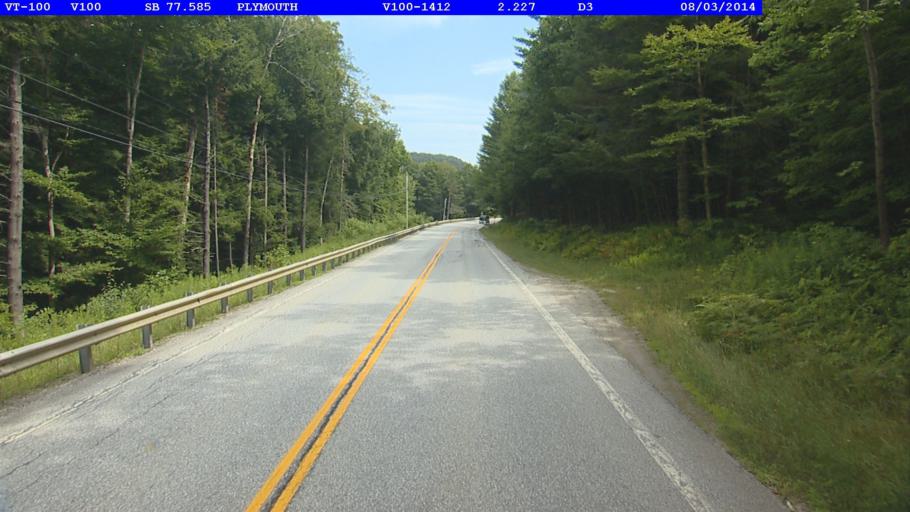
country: US
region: Vermont
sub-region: Windsor County
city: Woodstock
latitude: 43.4935
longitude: -72.7107
